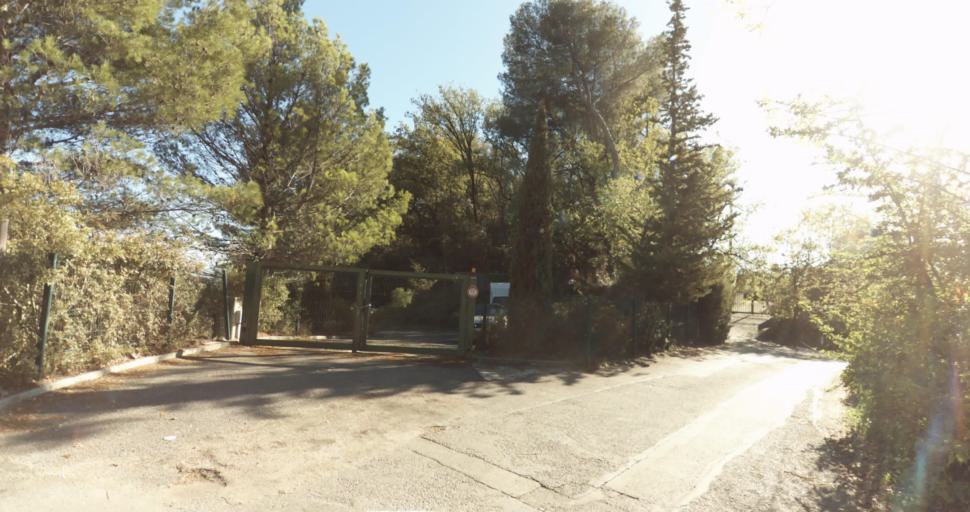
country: FR
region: Provence-Alpes-Cote d'Azur
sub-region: Departement des Alpes-Maritimes
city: Saint-Paul-de-Vence
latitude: 43.7028
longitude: 7.1309
